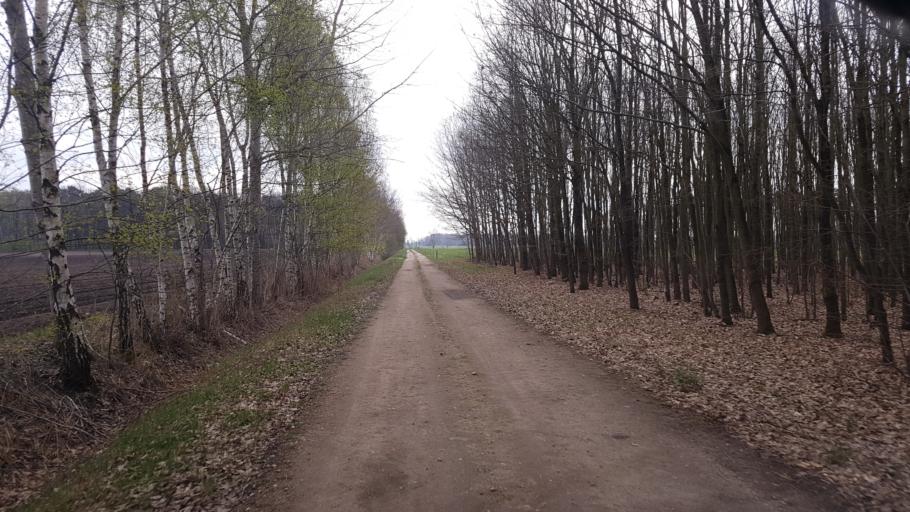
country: DE
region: Brandenburg
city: Bronkow
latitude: 51.6239
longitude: 13.8981
